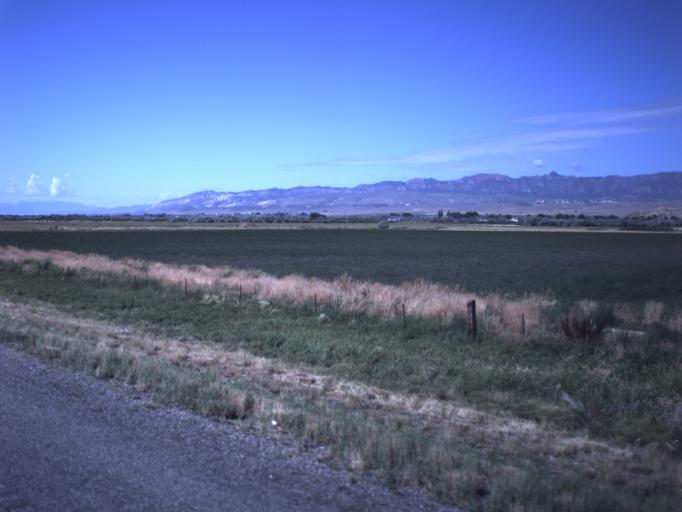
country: US
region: Utah
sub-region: Sevier County
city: Salina
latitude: 39.0054
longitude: -111.8386
